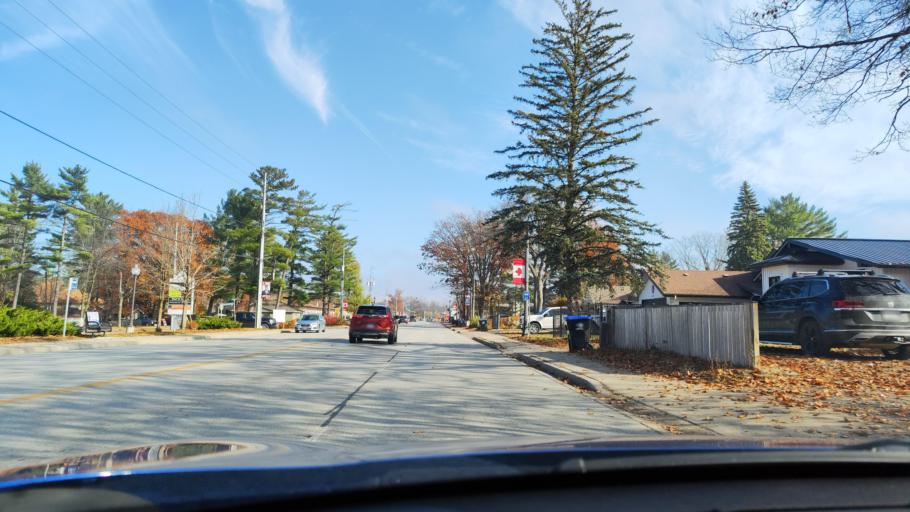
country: CA
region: Ontario
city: Wasaga Beach
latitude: 44.4871
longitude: -80.0546
